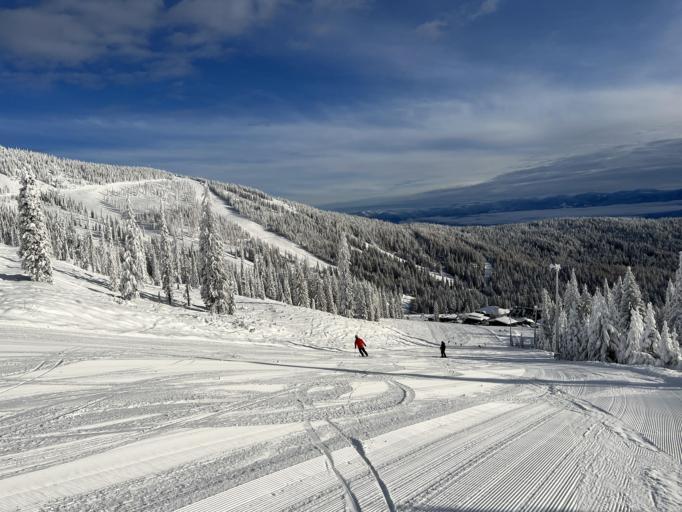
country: US
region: Idaho
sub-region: Bonner County
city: Ponderay
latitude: 48.3661
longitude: -116.6327
